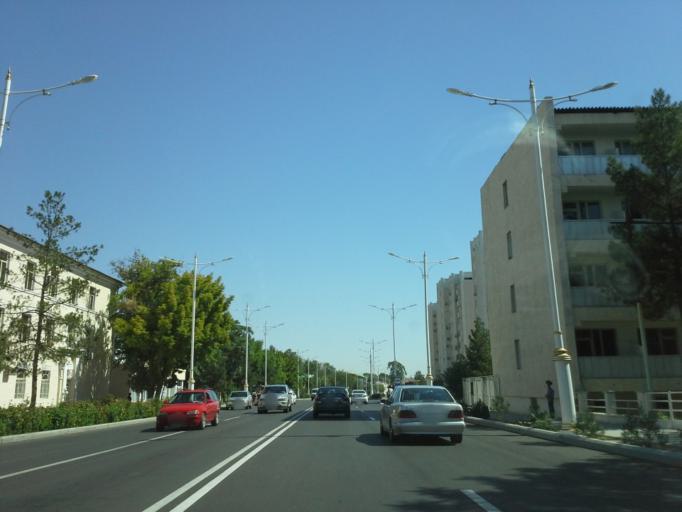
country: TM
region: Ahal
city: Ashgabat
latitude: 37.9515
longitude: 58.3549
